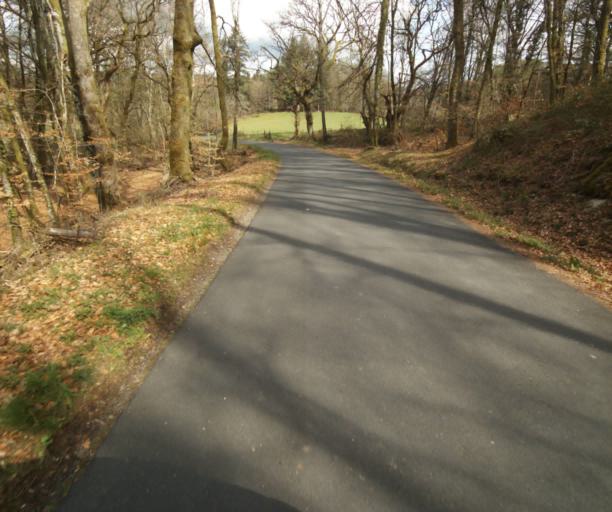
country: FR
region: Limousin
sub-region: Departement de la Correze
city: Correze
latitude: 45.3691
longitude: 1.8879
